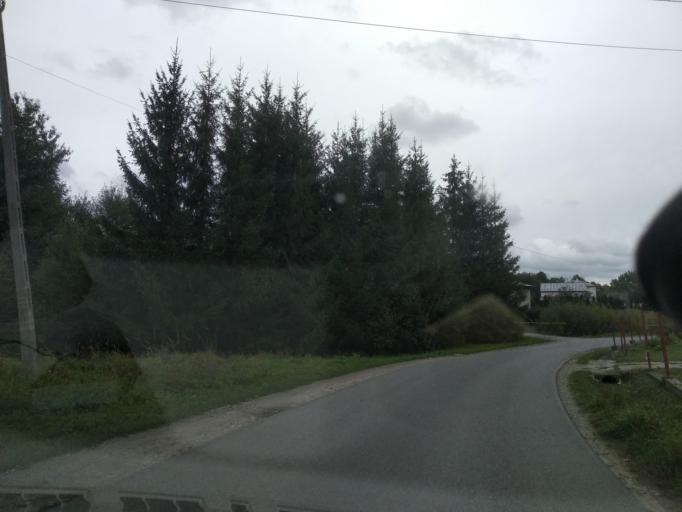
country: PL
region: Subcarpathian Voivodeship
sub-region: Powiat krosnienski
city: Dukla
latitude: 49.5452
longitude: 21.7320
